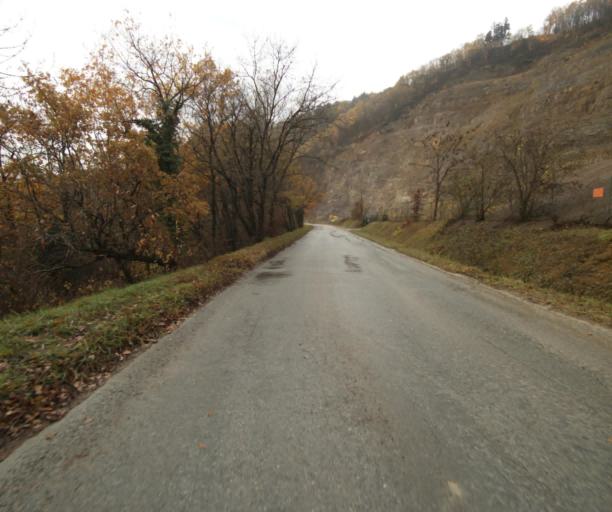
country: FR
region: Limousin
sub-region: Departement de la Correze
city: Cornil
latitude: 45.1953
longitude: 1.6517
